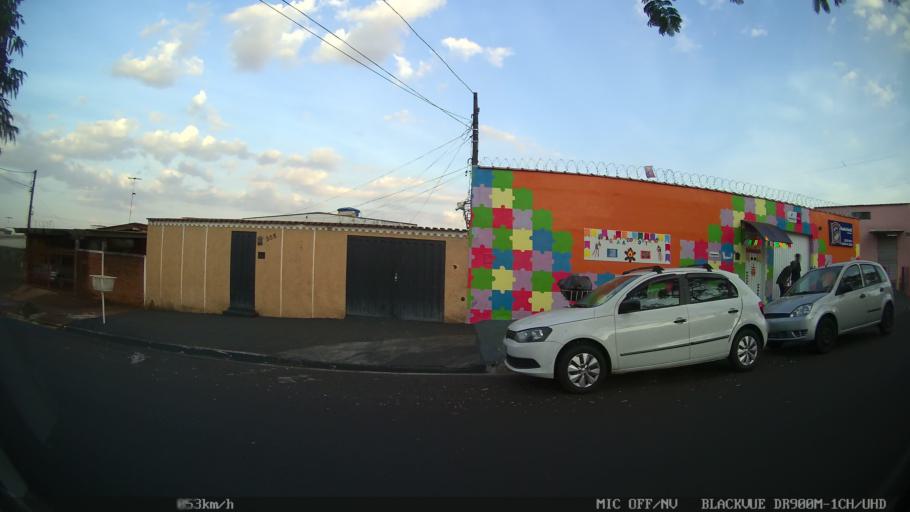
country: BR
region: Sao Paulo
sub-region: Ribeirao Preto
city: Ribeirao Preto
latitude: -21.1332
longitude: -47.8426
